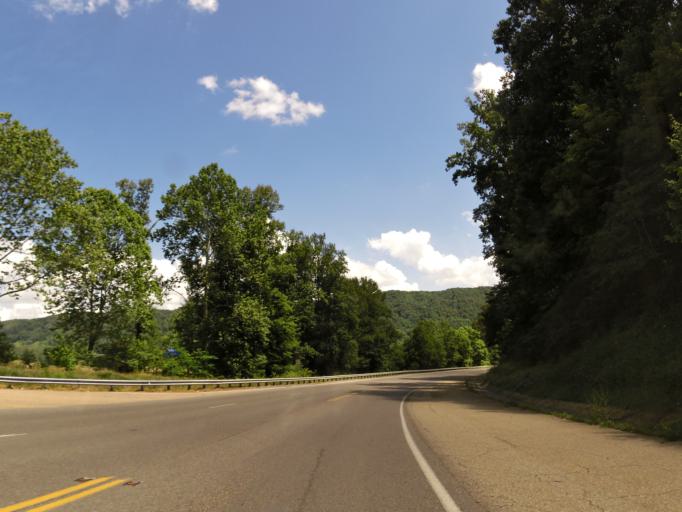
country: US
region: Virginia
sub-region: Lee County
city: Dryden
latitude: 36.7185
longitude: -82.9112
